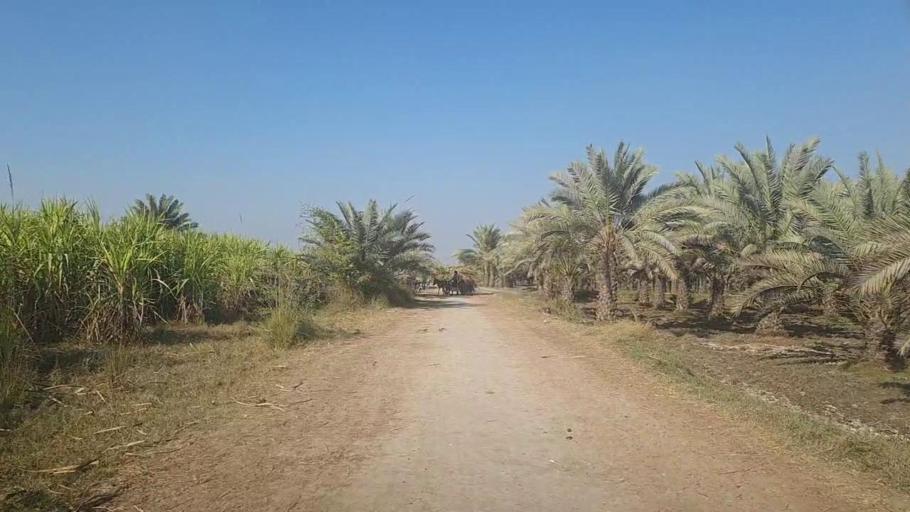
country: PK
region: Sindh
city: Kot Diji
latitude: 27.4320
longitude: 68.7376
